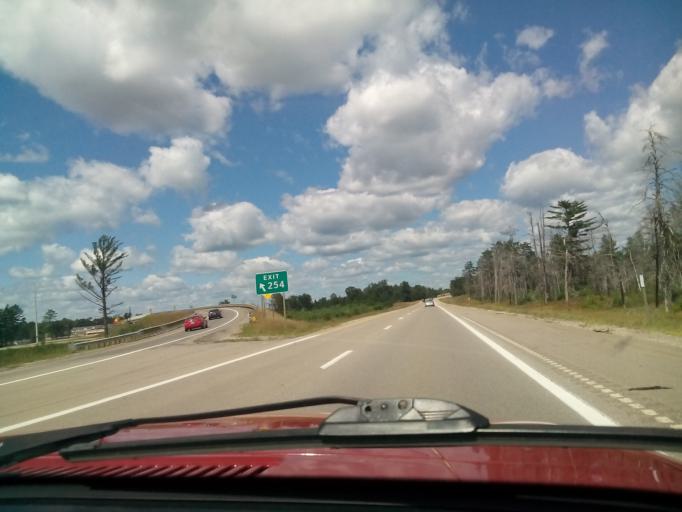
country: US
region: Michigan
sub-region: Crawford County
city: Grayling
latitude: 44.6423
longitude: -84.7068
